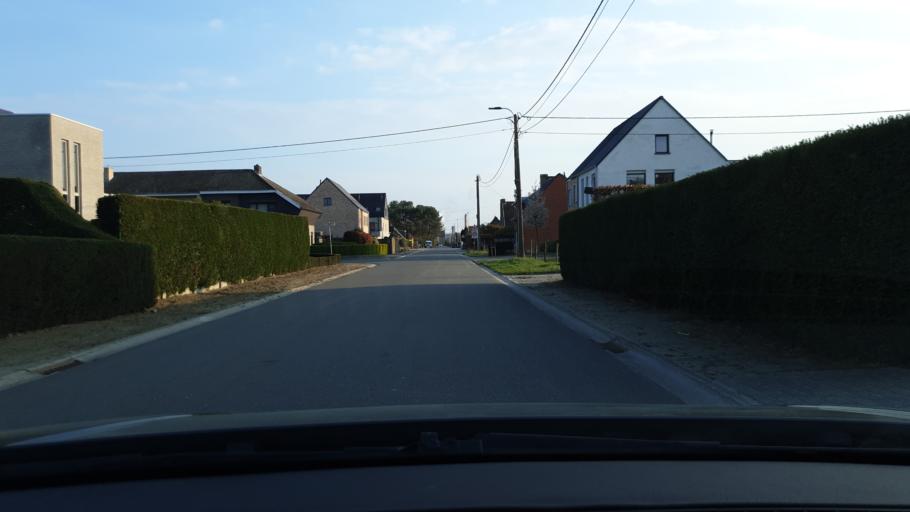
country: BE
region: Flanders
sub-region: Provincie Antwerpen
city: Geel
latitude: 51.1288
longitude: 5.0076
